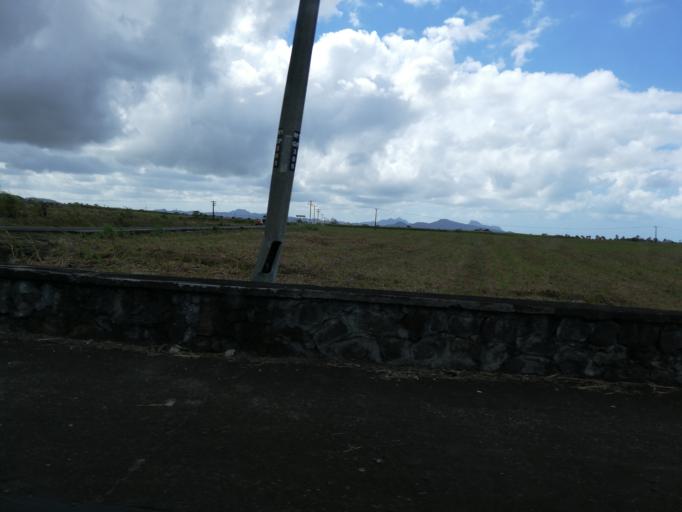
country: MU
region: Grand Port
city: New Grove
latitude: -20.4280
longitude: 57.6172
